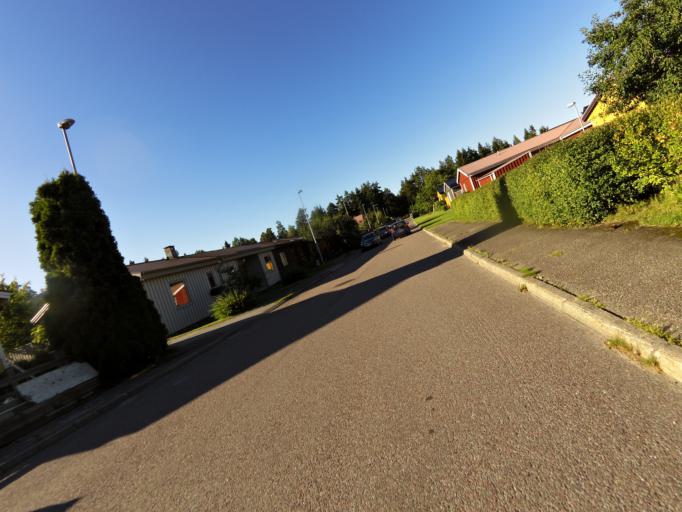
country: SE
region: Gaevleborg
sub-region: Gavle Kommun
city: Gavle
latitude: 60.6534
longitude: 17.1487
